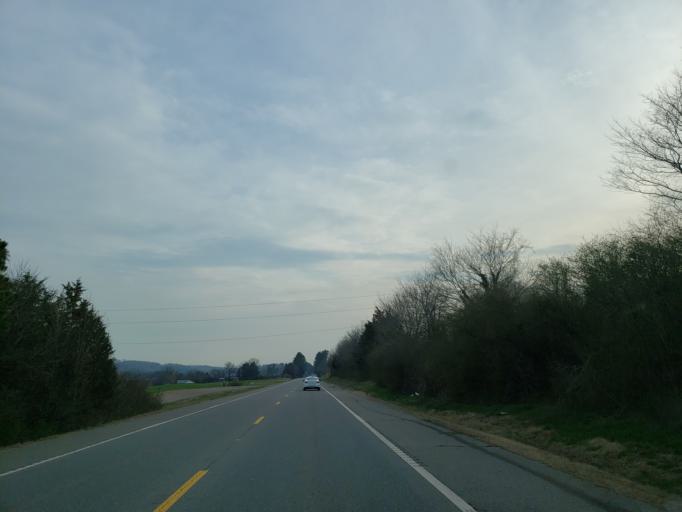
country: US
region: Tennessee
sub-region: Bradley County
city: Wildwood Lake
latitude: 35.0459
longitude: -84.9028
